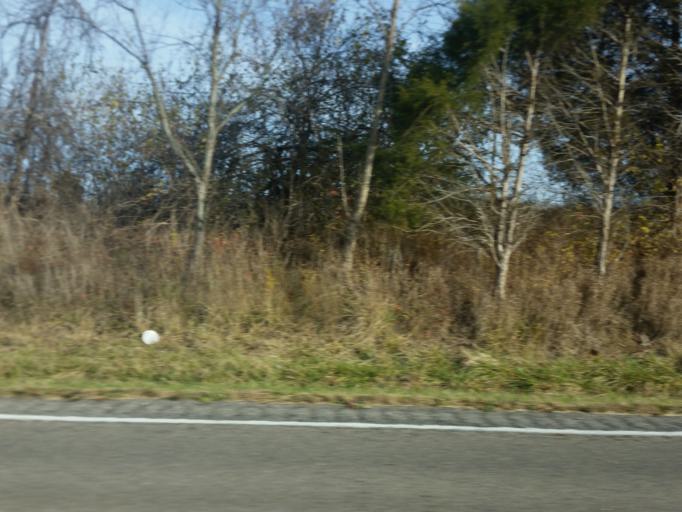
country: US
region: Kentucky
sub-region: Pendleton County
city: Falmouth
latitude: 38.6064
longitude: -84.3039
